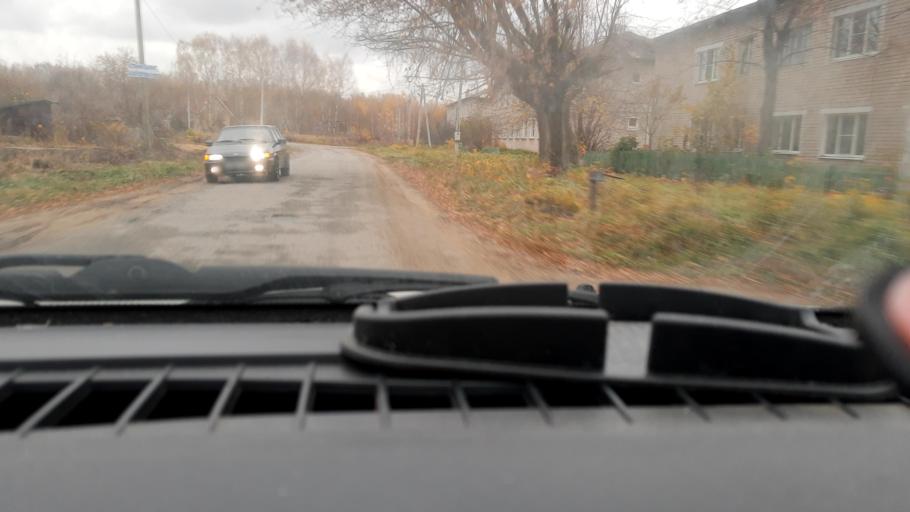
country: RU
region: Nizjnij Novgorod
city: Sitniki
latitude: 56.4119
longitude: 44.0347
